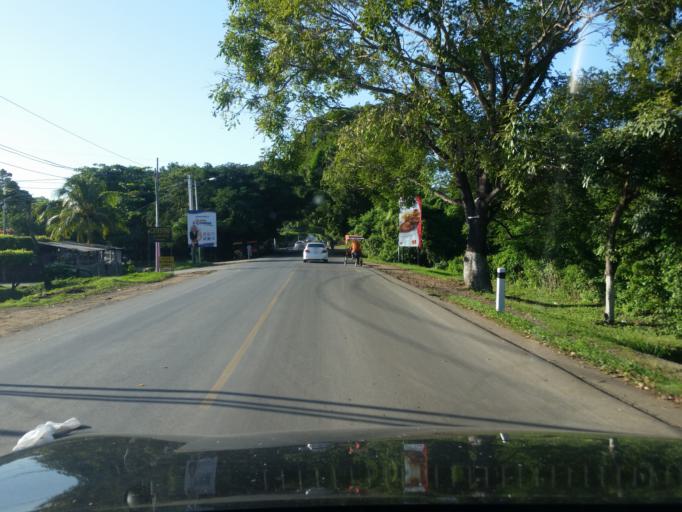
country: NI
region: Rivas
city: Rivas
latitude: 11.4378
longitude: -85.8195
